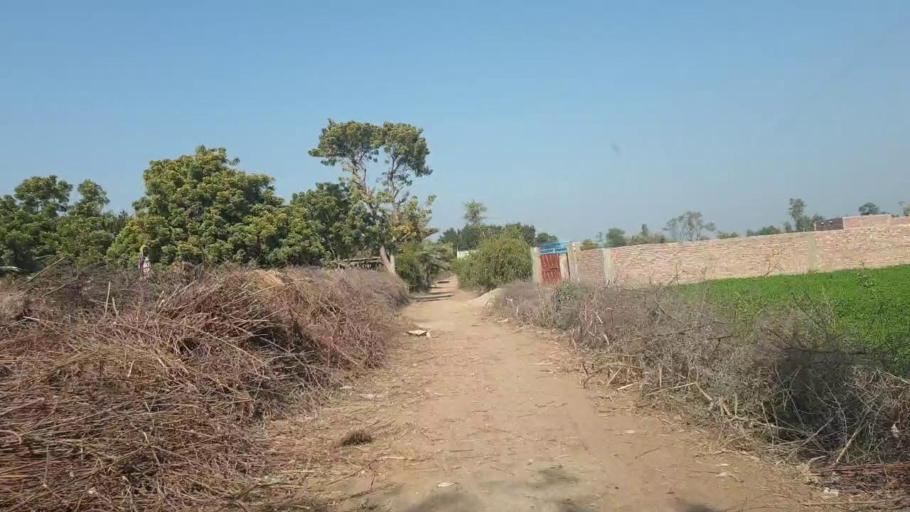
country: PK
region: Sindh
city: Shahdadpur
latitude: 26.0508
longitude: 68.4615
